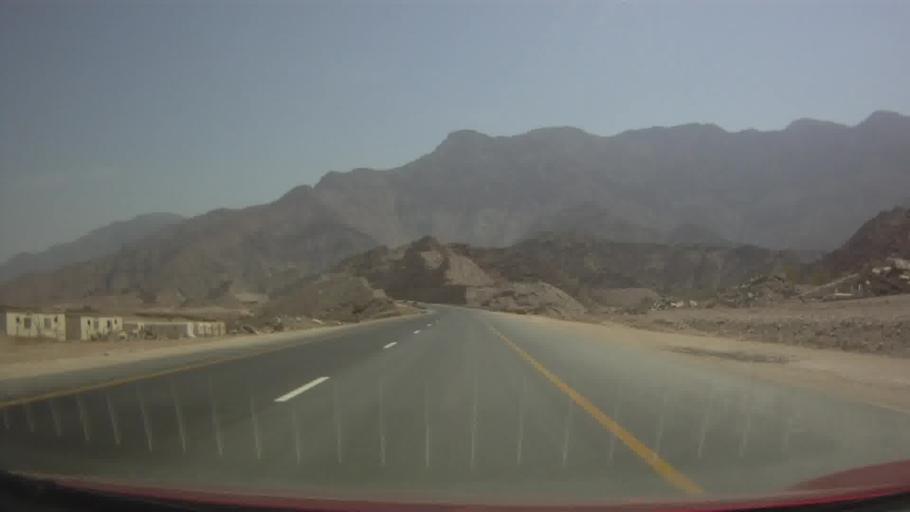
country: OM
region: Muhafazat Masqat
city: Muscat
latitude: 23.4022
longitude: 58.7812
